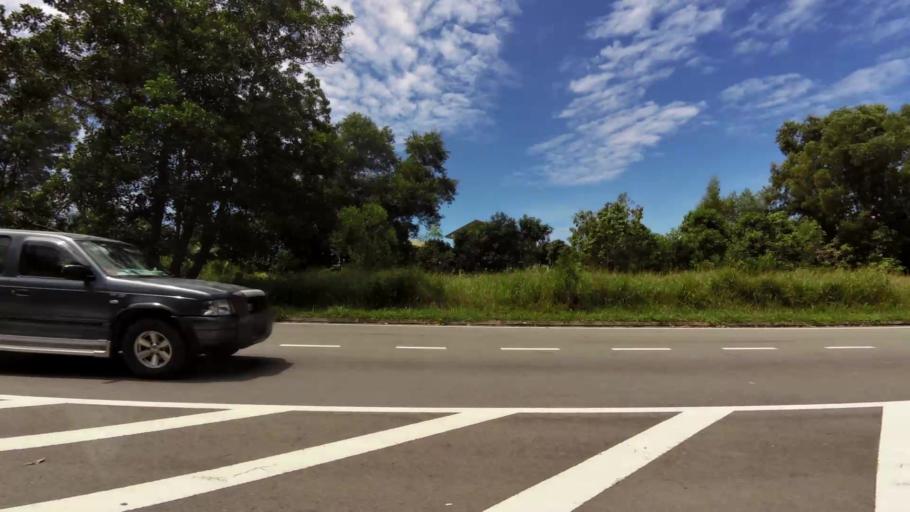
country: BN
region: Brunei and Muara
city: Bandar Seri Begawan
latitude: 4.9974
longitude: 115.0148
